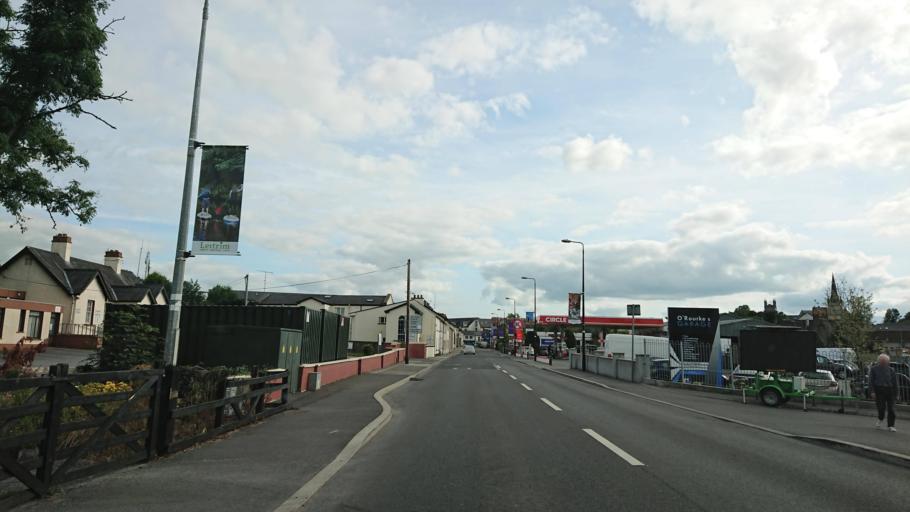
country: IE
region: Connaught
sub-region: County Leitrim
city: Carrick-on-Shannon
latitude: 53.9495
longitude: -8.0913
